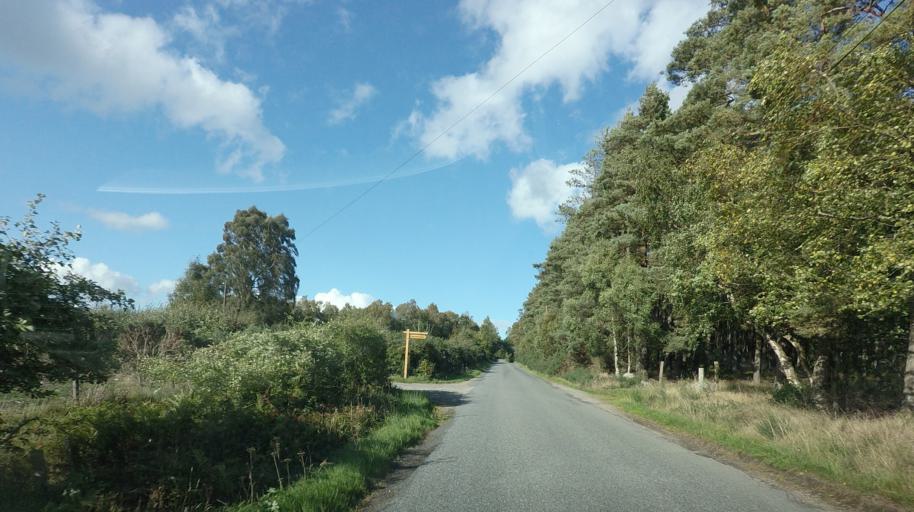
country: GB
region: Scotland
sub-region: Aberdeenshire
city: Banchory
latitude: 57.0709
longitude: -2.4653
